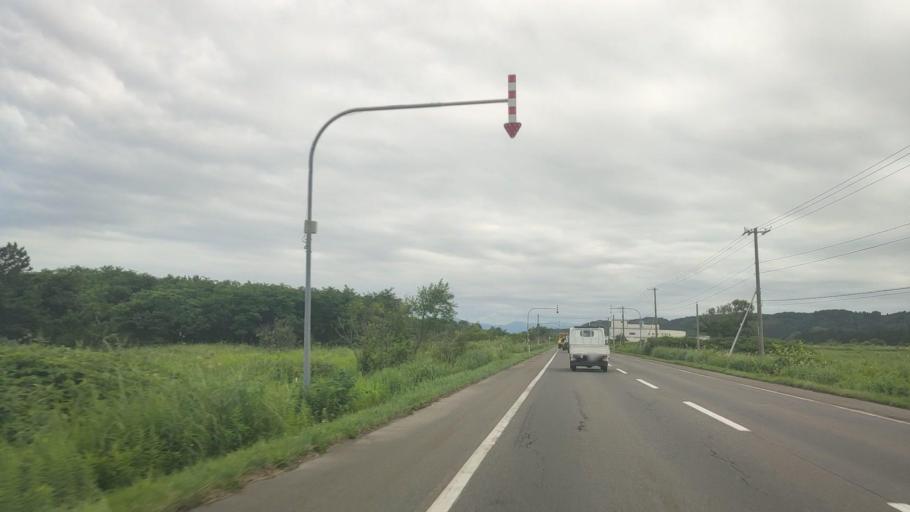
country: JP
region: Hokkaido
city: Niseko Town
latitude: 42.3911
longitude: 140.2985
